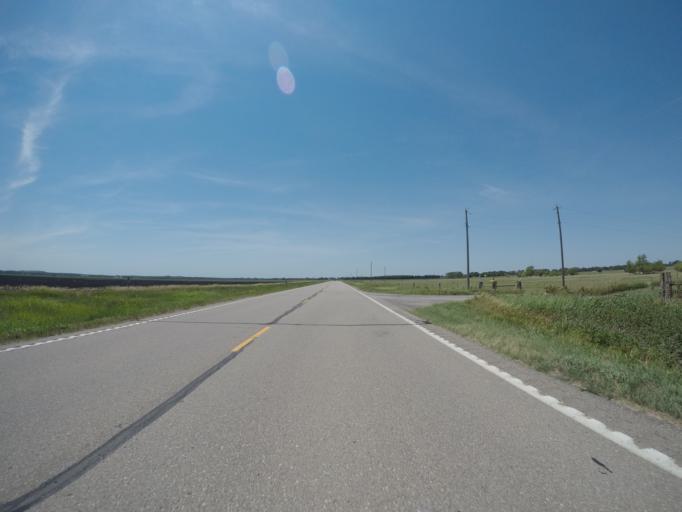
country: US
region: Kansas
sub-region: Ottawa County
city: Minneapolis
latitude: 39.0306
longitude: -97.5622
